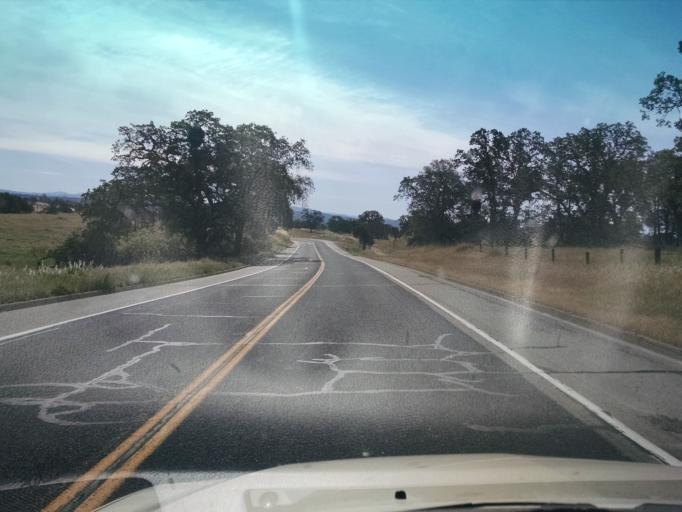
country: US
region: California
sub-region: Madera County
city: Yosemite Lakes
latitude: 37.1211
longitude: -119.7107
